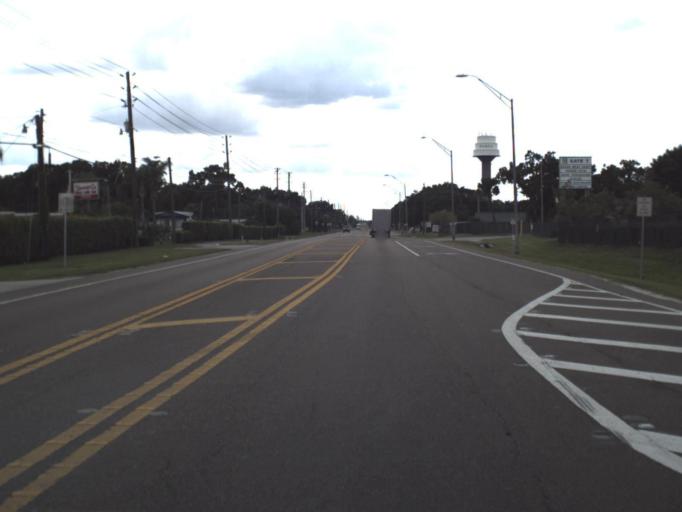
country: US
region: Florida
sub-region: Polk County
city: Winston
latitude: 28.0395
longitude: -82.0023
